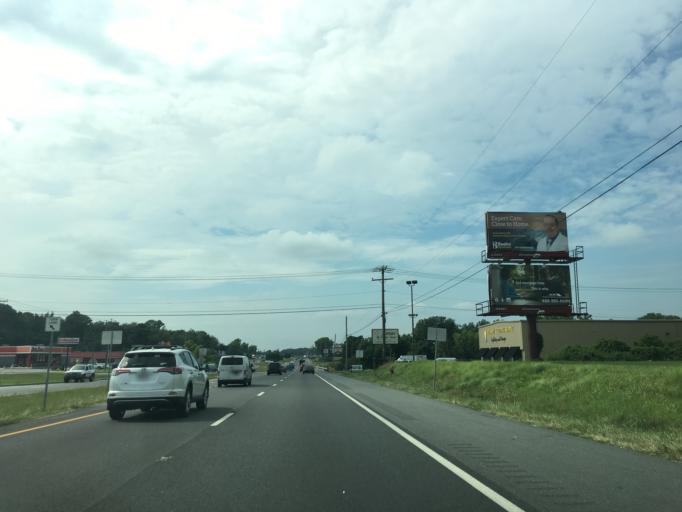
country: US
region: Delaware
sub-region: Sussex County
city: Millsboro
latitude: 38.5761
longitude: -75.2867
